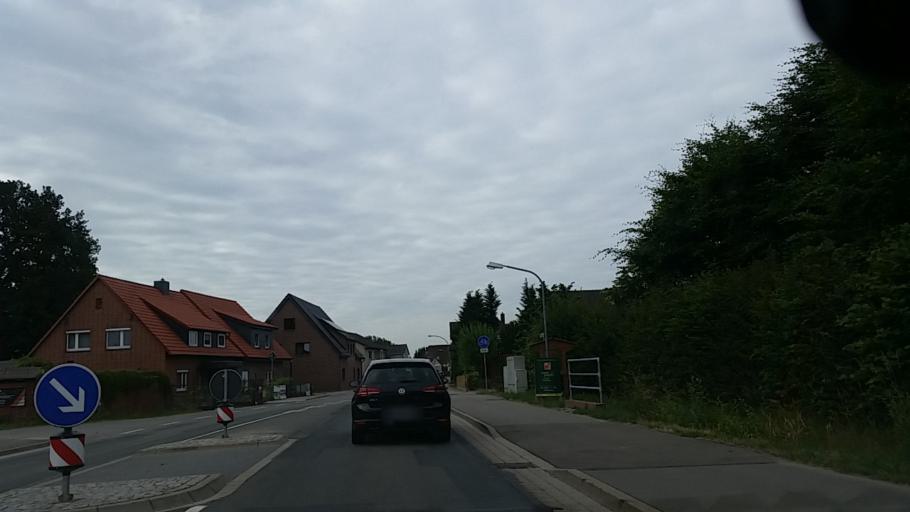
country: DE
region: Lower Saxony
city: Tappenbeck
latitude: 52.4763
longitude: 10.7430
